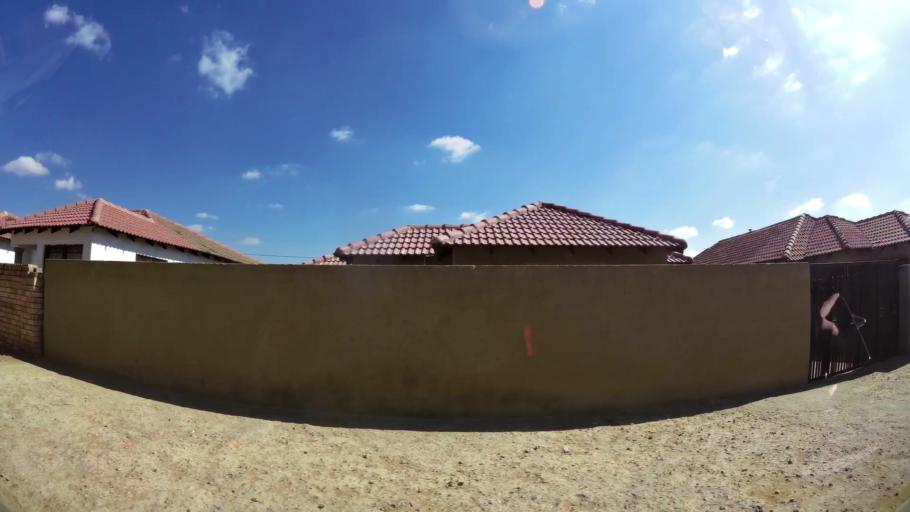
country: ZA
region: Gauteng
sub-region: West Rand District Municipality
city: Krugersdorp
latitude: -26.1478
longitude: 27.7733
